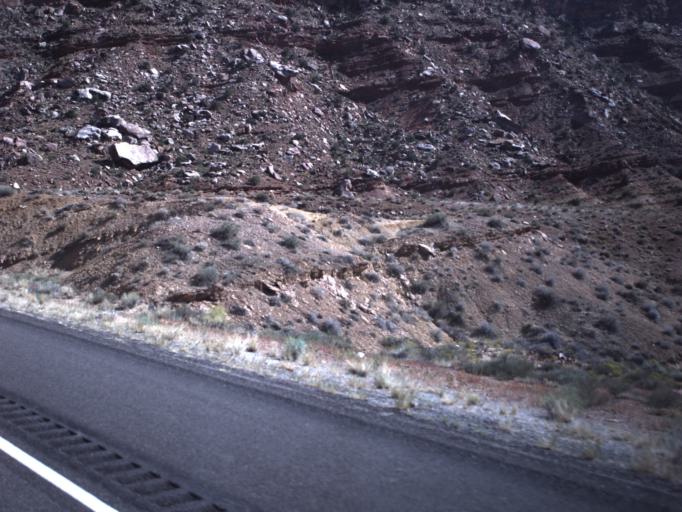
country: US
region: Utah
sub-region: Carbon County
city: East Carbon City
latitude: 38.9249
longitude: -110.4526
